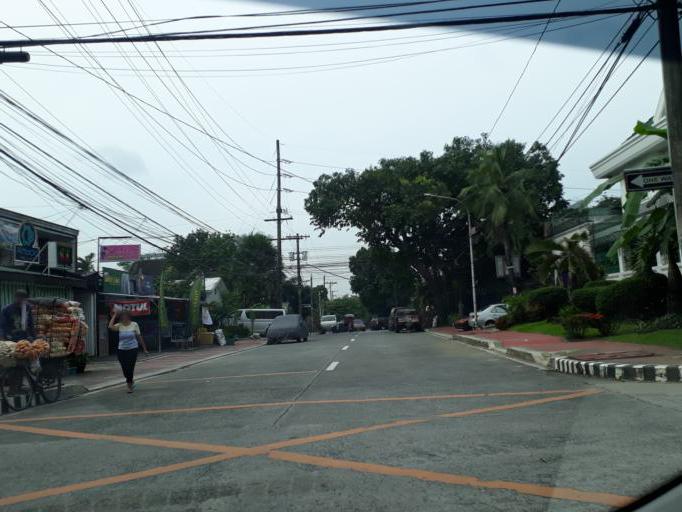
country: PH
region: Calabarzon
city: Del Monte
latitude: 14.6347
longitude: 121.0288
